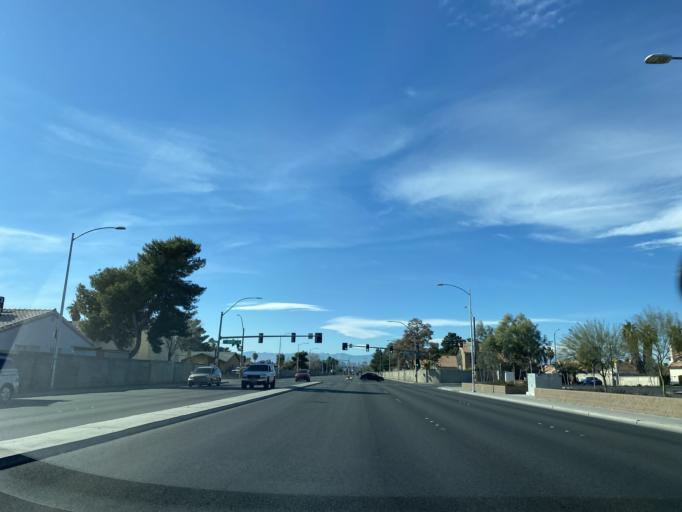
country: US
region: Nevada
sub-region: Clark County
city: Sunrise Manor
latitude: 36.1738
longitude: -115.0703
